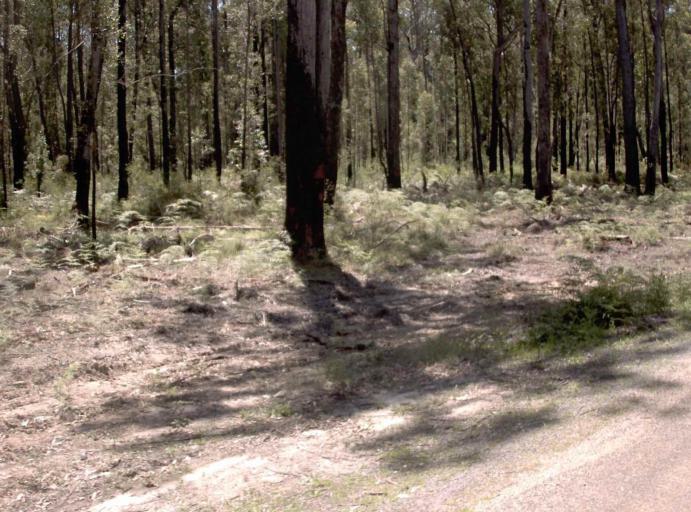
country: AU
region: Victoria
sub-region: East Gippsland
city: Lakes Entrance
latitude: -37.6897
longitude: 148.7500
